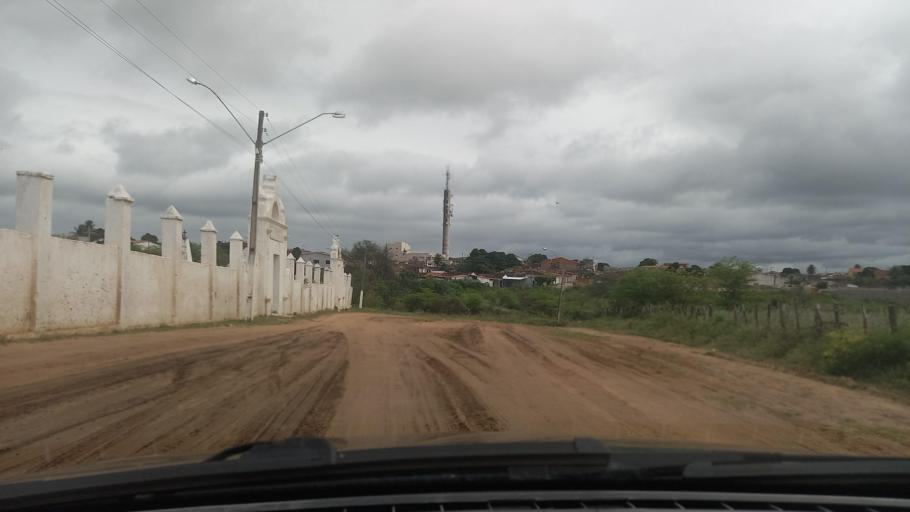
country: BR
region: Alagoas
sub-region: Delmiro Gouveia
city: Delmiro Gouveia
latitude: -9.3897
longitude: -37.9943
